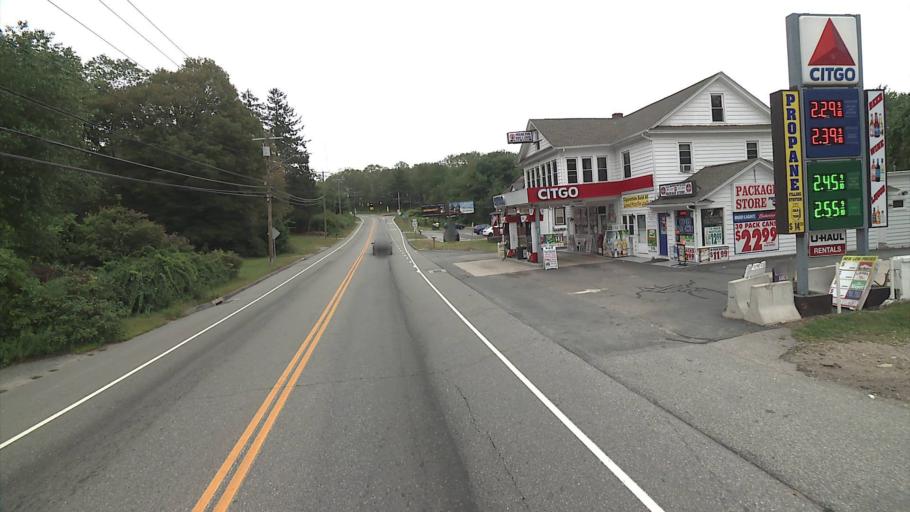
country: US
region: Connecticut
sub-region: New London County
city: Montville Center
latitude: 41.4289
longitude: -72.2167
